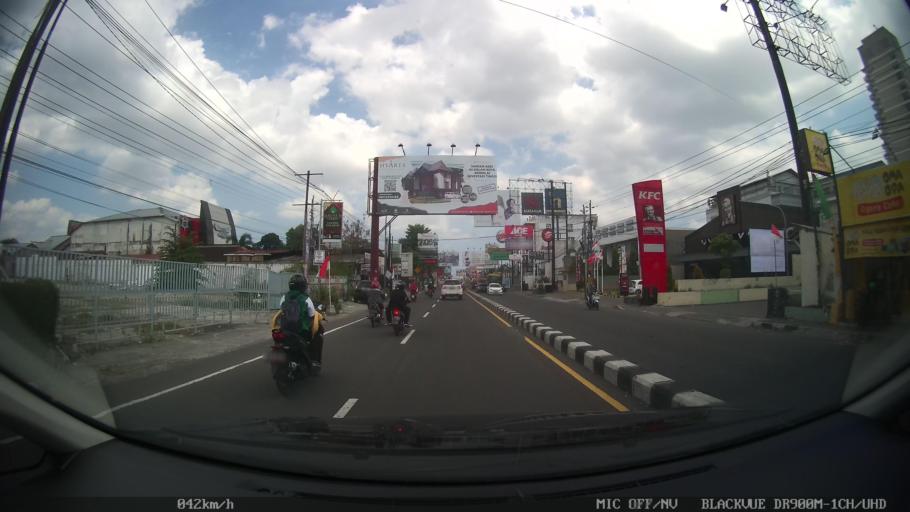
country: ID
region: Daerah Istimewa Yogyakarta
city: Melati
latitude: -7.7524
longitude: 110.3623
